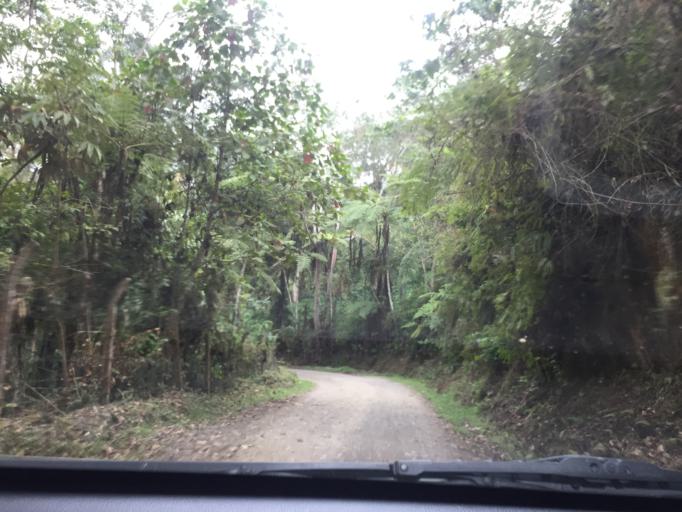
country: CO
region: Cundinamarca
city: Bojaca
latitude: 4.6871
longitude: -74.3747
